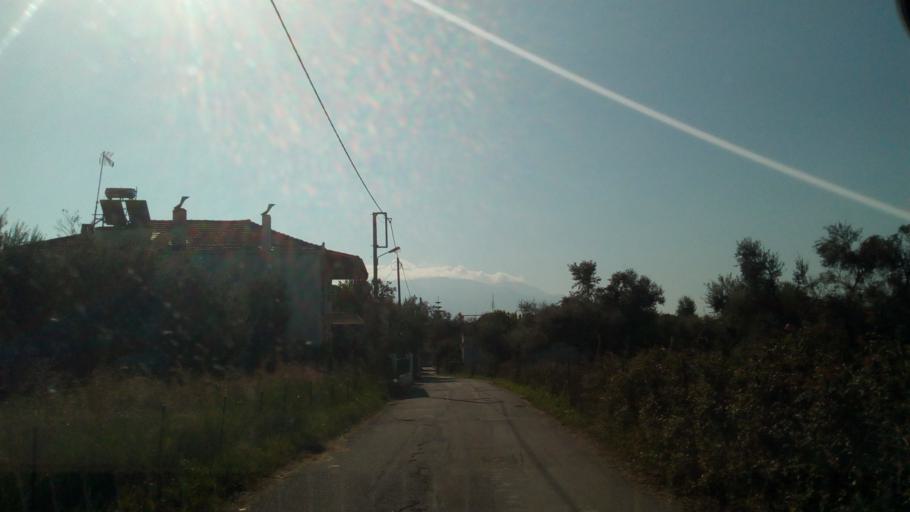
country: GR
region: West Greece
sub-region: Nomos Aitolias kai Akarnanias
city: Nafpaktos
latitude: 38.3823
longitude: 21.7995
